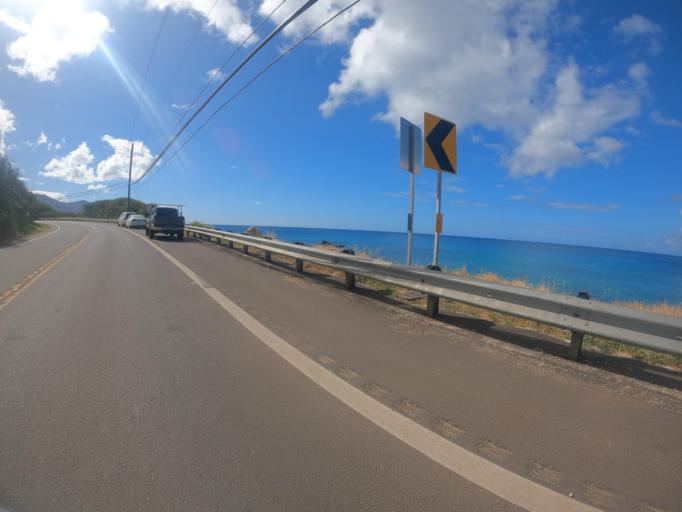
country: US
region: Hawaii
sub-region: Honolulu County
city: Makaha Valley
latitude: 21.5458
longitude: -158.2404
